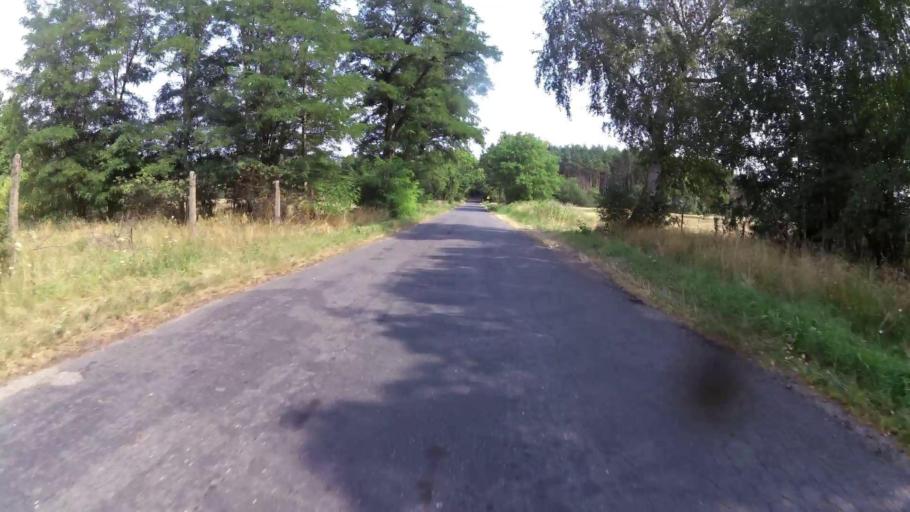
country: PL
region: West Pomeranian Voivodeship
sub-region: Powiat mysliborski
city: Mysliborz
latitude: 52.8433
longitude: 14.8038
